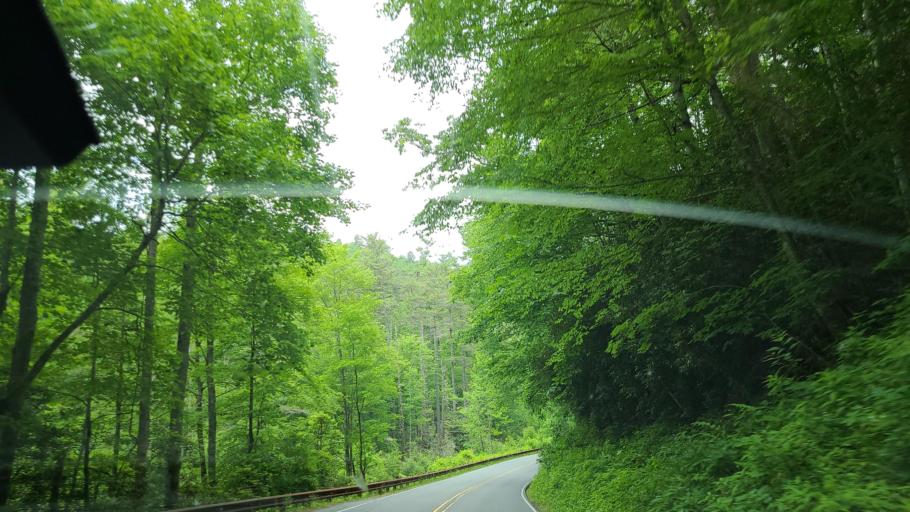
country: US
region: North Carolina
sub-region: Macon County
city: Franklin
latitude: 35.0892
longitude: -83.2680
